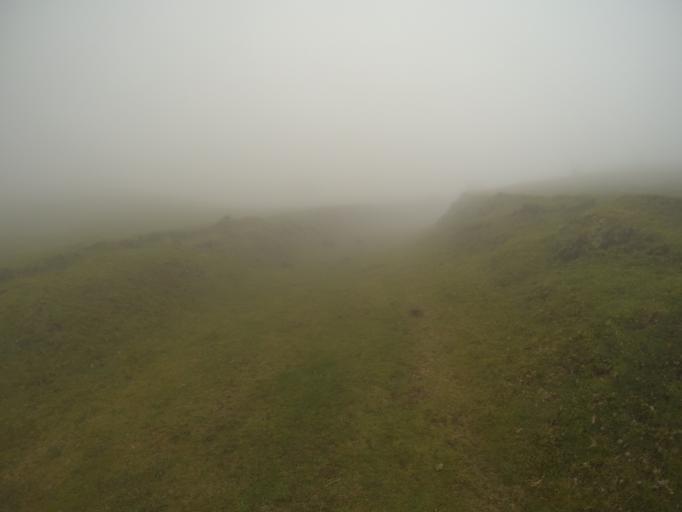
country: PT
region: Madeira
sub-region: Porto Moniz
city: Porto Moniz
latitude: 32.8105
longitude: -17.1415
